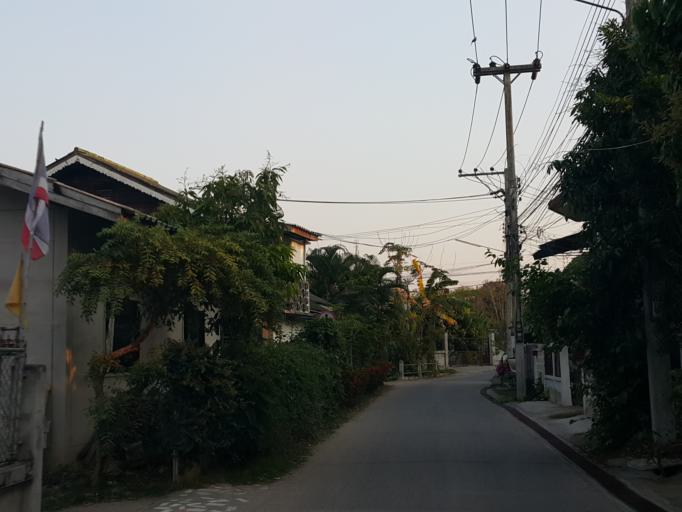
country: TH
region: Chiang Mai
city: San Sai
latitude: 18.8936
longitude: 98.9608
